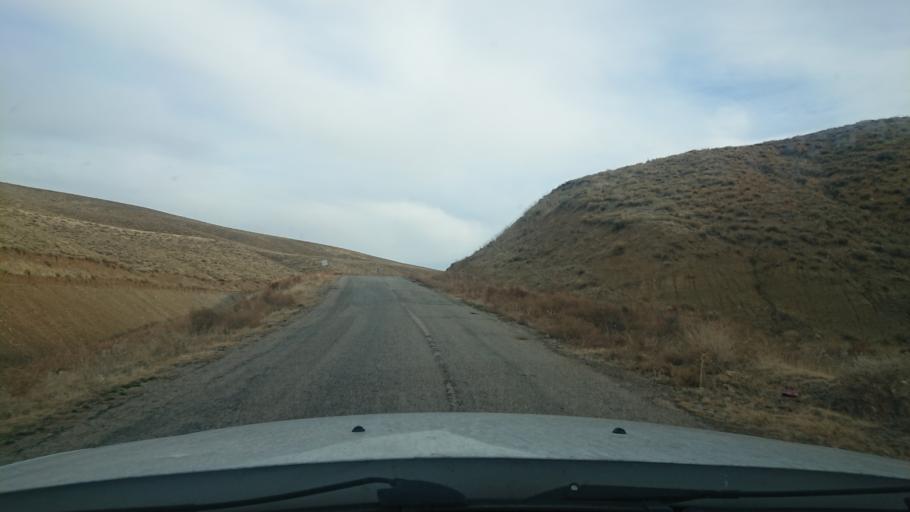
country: TR
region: Aksaray
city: Acipinar
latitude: 38.6291
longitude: 33.7997
